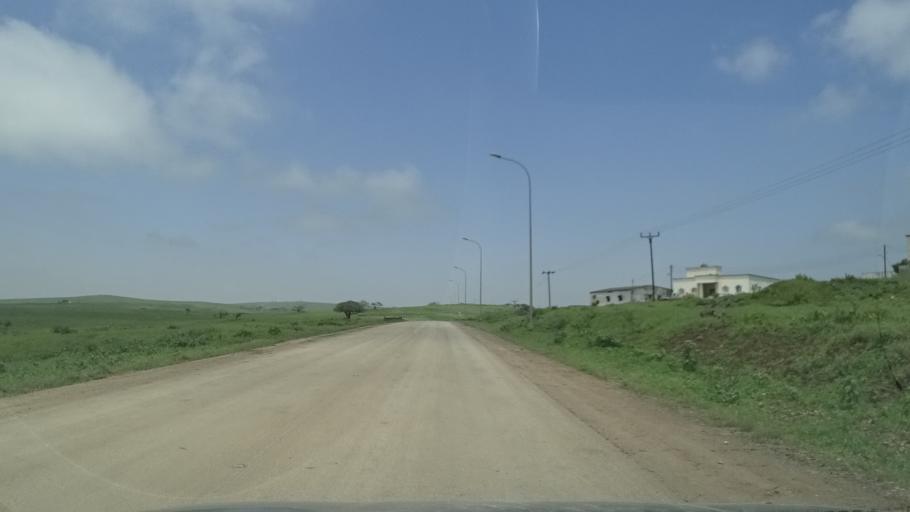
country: OM
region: Zufar
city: Salalah
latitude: 17.2151
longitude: 54.2492
